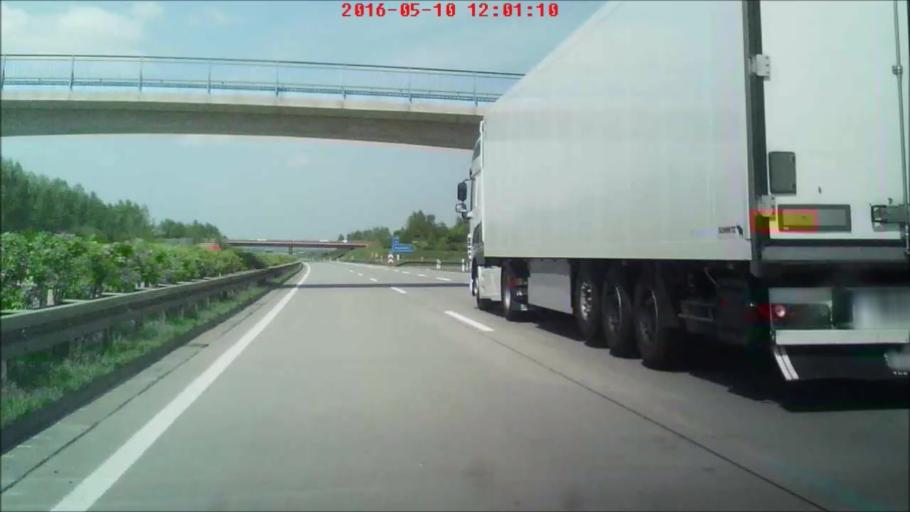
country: DE
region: Thuringia
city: Ingersleben
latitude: 50.9516
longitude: 10.9464
